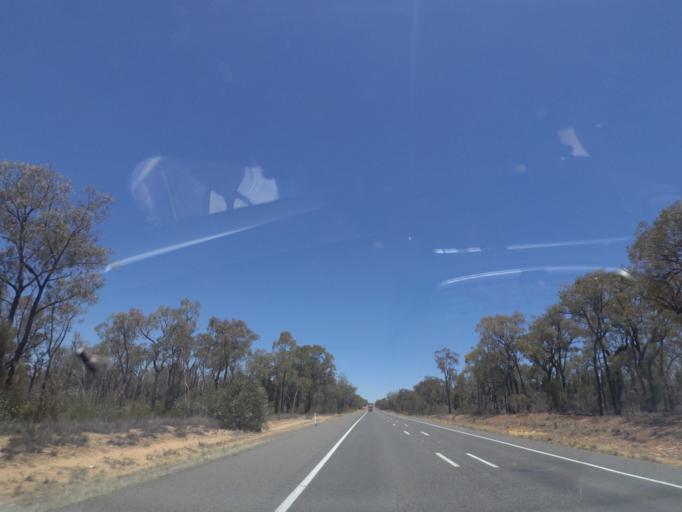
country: AU
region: New South Wales
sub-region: Warrumbungle Shire
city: Coonabarabran
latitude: -30.9114
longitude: 149.4358
